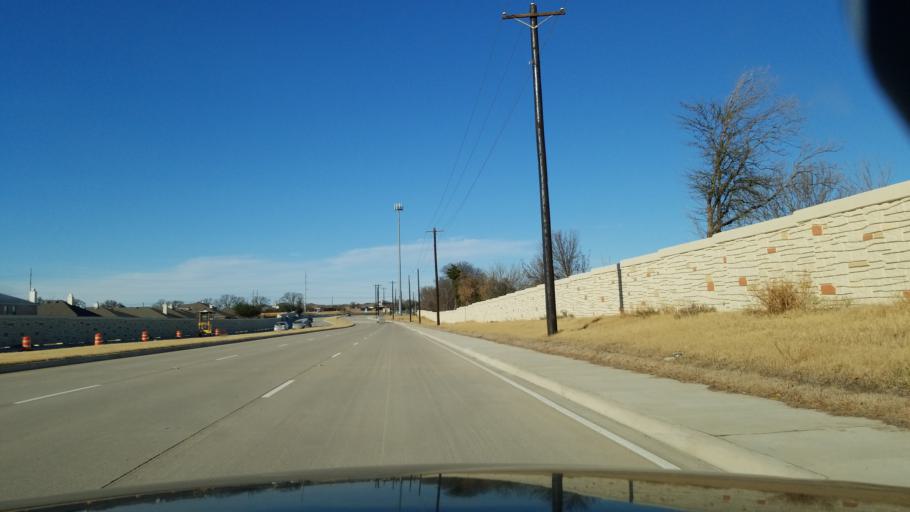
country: US
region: Texas
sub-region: Denton County
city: Corinth
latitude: 33.1473
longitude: -97.0973
